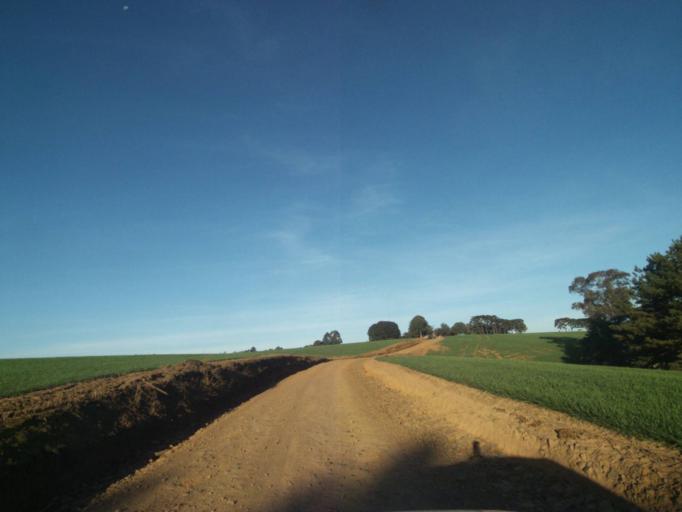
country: BR
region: Parana
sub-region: Telemaco Borba
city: Telemaco Borba
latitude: -24.4707
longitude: -50.5903
